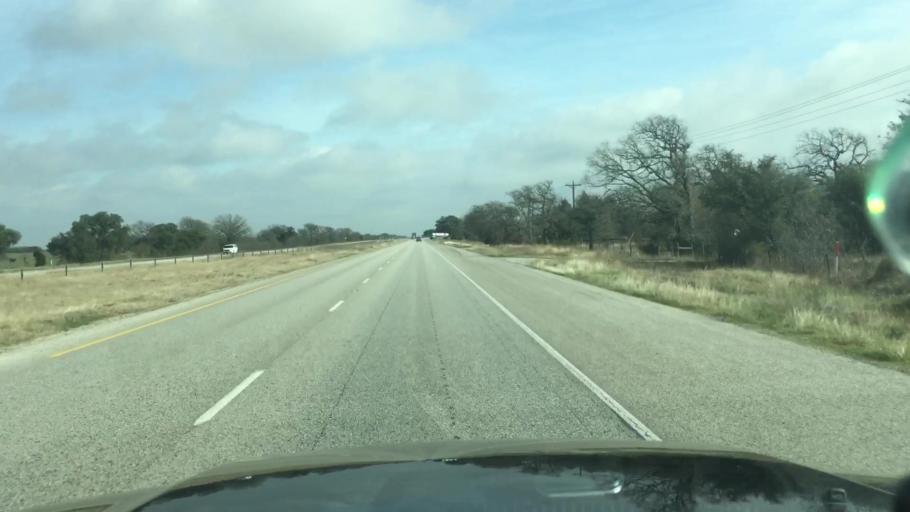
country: US
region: Texas
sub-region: Lee County
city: Giddings
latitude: 30.1737
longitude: -96.8827
